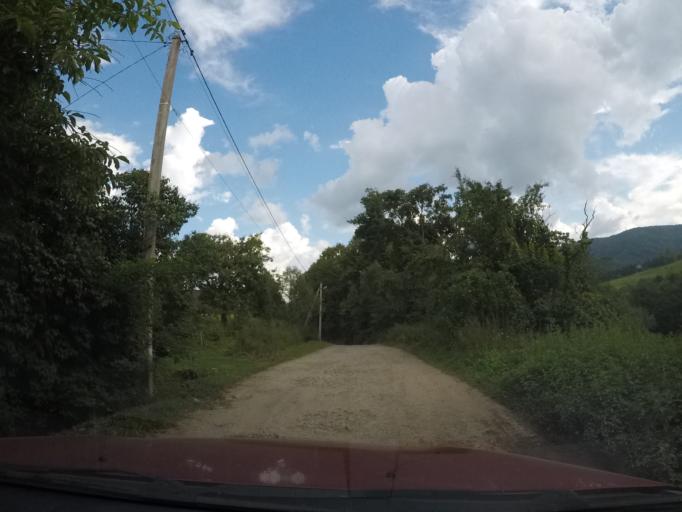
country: UA
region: Zakarpattia
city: Velykyi Bereznyi
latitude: 49.0318
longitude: 22.5845
